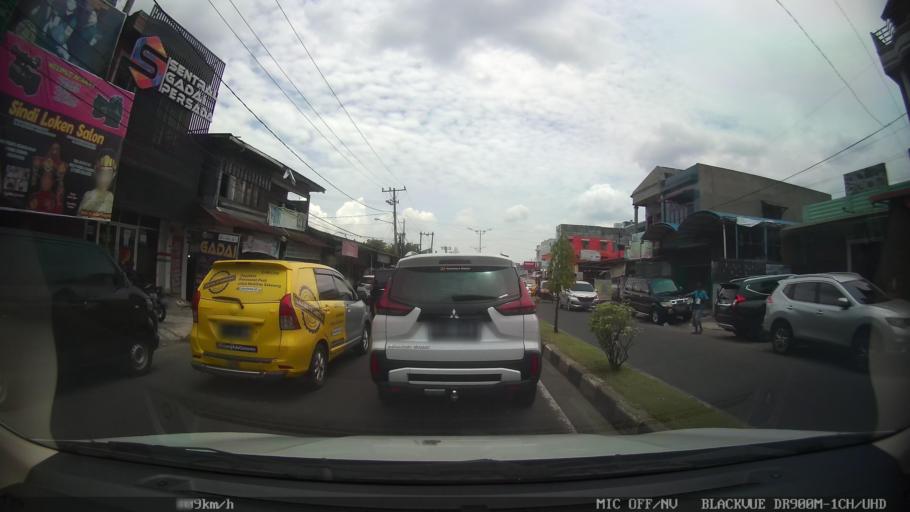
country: ID
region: North Sumatra
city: Medan
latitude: 3.5420
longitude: 98.6554
